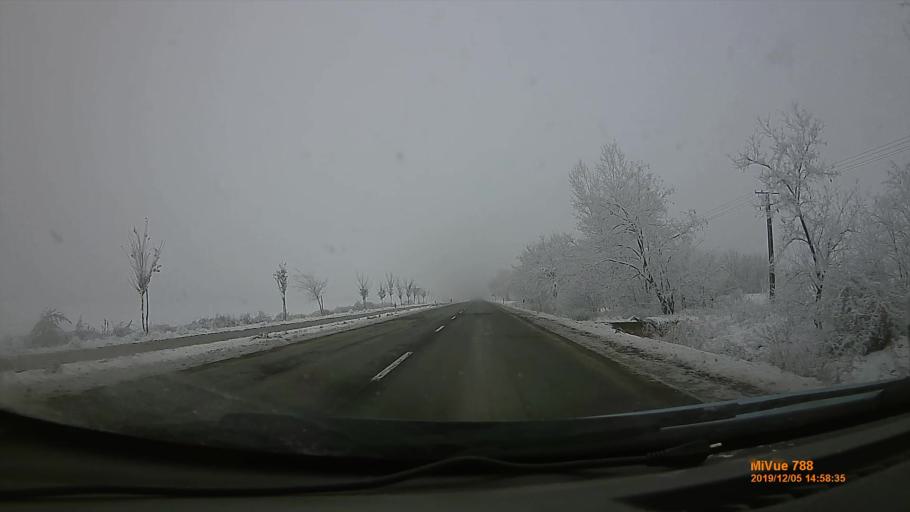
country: HU
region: Szabolcs-Szatmar-Bereg
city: Nyirtelek
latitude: 48.0498
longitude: 21.5694
